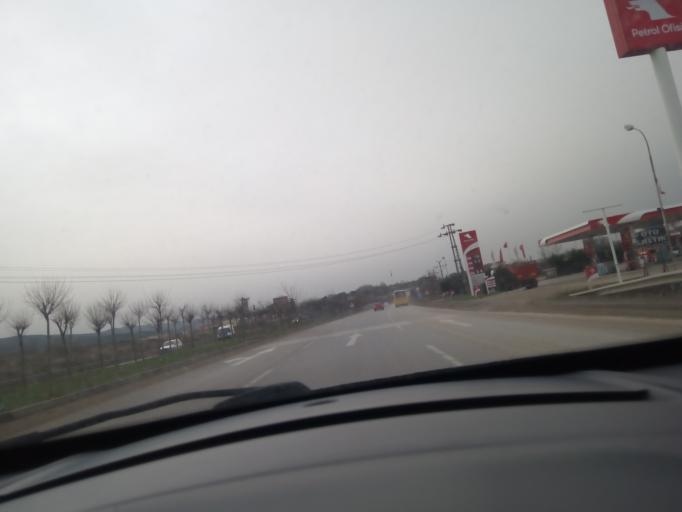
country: TR
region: Balikesir
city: Susurluk
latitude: 39.9549
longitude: 28.1710
